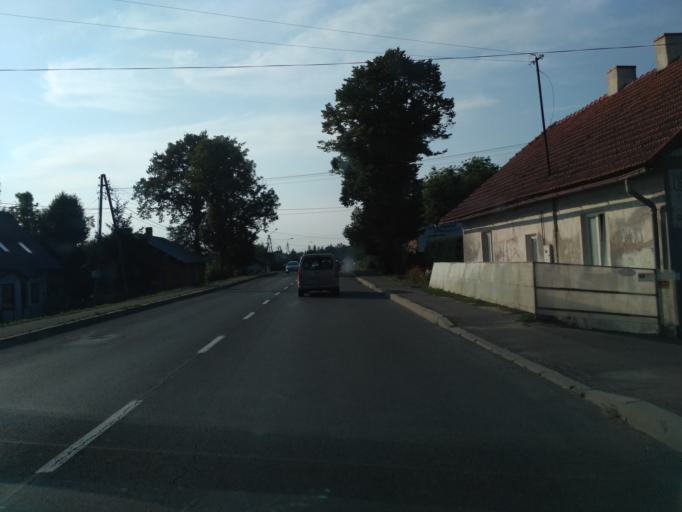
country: PL
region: Subcarpathian Voivodeship
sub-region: Powiat brzozowski
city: Humniska
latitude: 49.6805
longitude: 22.0447
